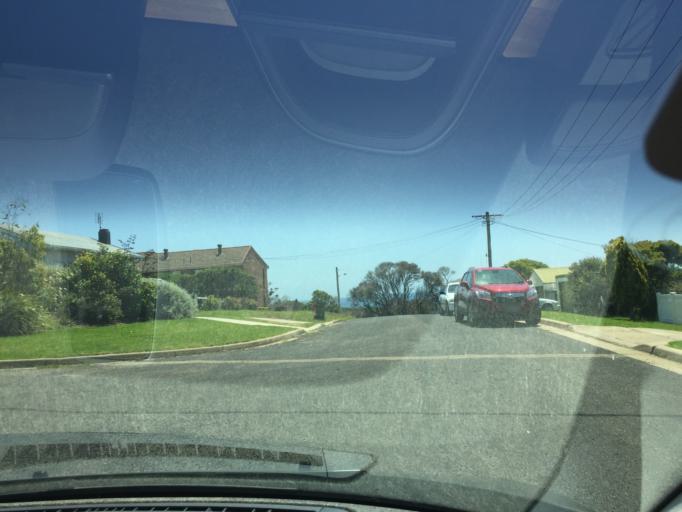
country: AU
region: New South Wales
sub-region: Bega Valley
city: Bega
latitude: -36.7301
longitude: 149.9877
